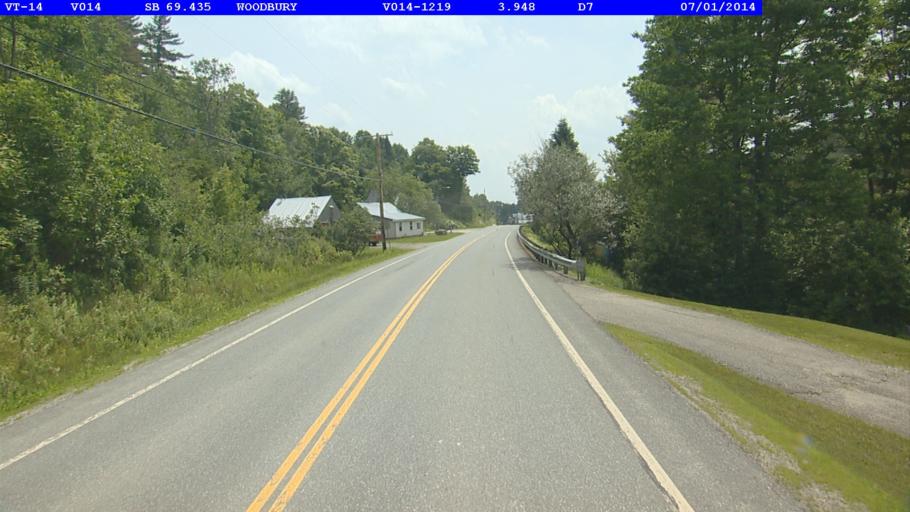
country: US
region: Vermont
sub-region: Caledonia County
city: Hardwick
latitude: 44.4448
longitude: -72.4159
